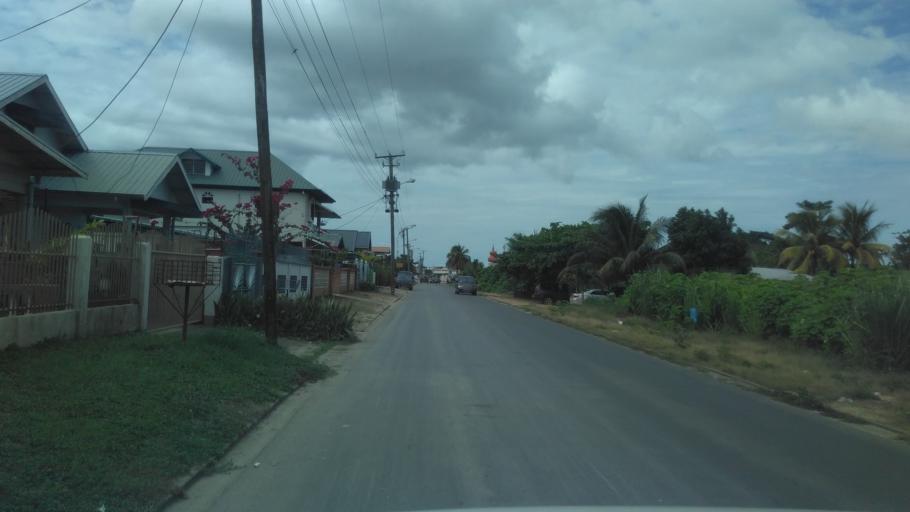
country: SR
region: Paramaribo
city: Paramaribo
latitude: 5.8481
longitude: -55.1257
